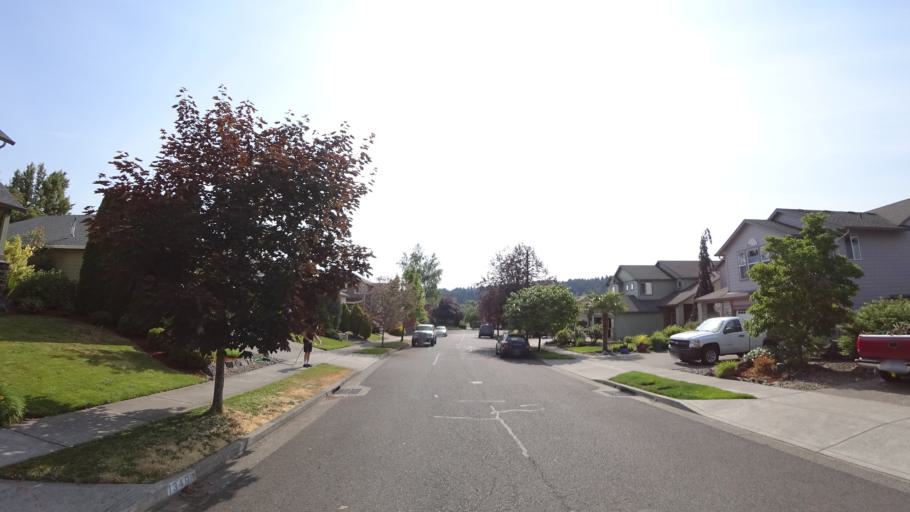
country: US
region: Oregon
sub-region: Clackamas County
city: Happy Valley
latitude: 45.4519
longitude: -122.5247
